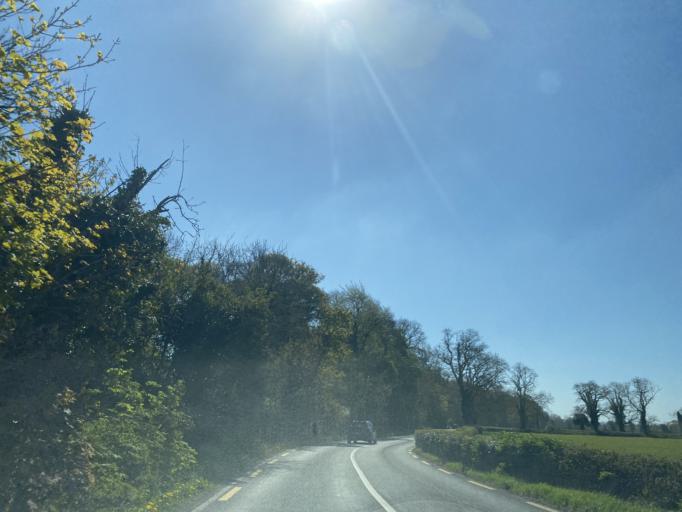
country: IE
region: Leinster
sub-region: Kildare
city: Kill
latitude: 53.2621
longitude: -6.5866
